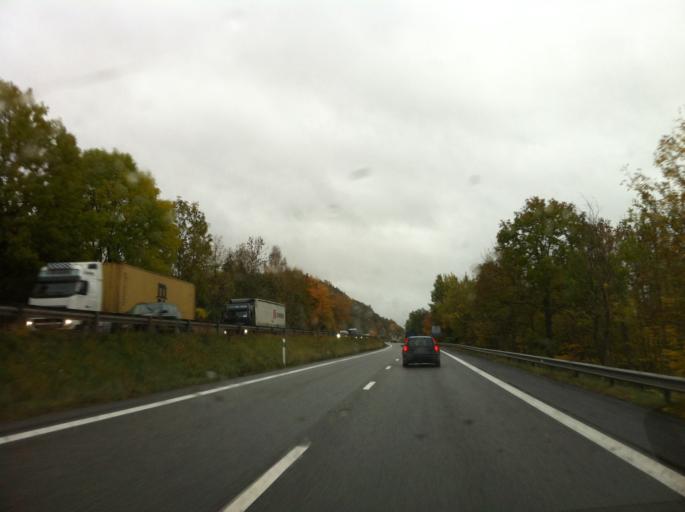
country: SE
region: Joenkoeping
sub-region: Jonkopings Kommun
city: Kaxholmen
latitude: 57.8439
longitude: 14.2679
